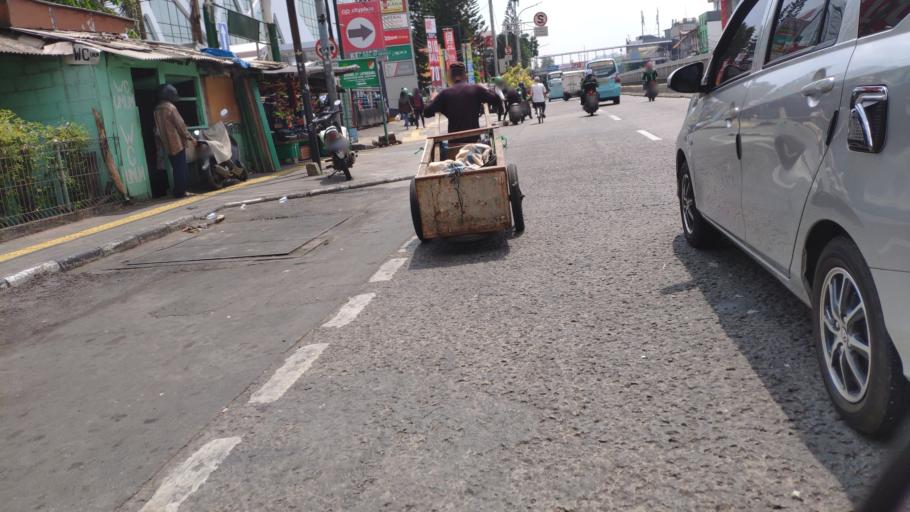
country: ID
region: Jakarta Raya
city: Jakarta
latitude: -6.2141
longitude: 106.8636
